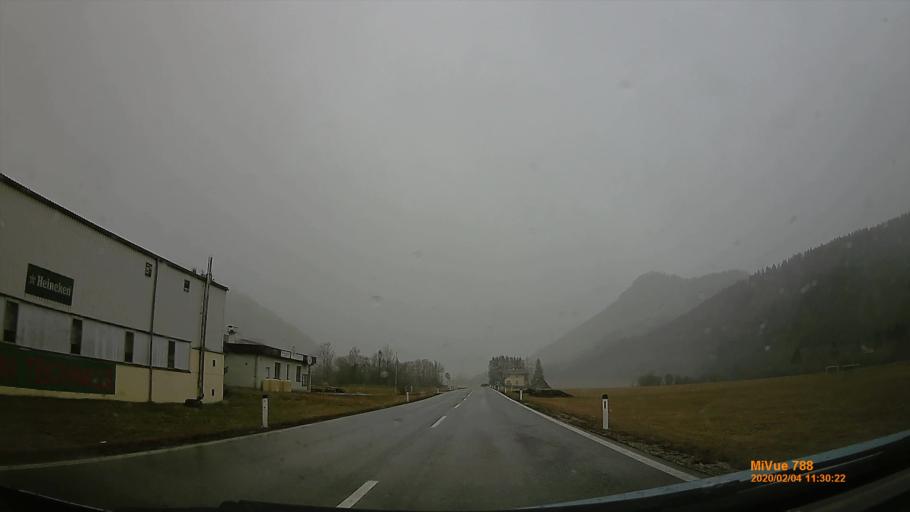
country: AT
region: Styria
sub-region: Politischer Bezirk Bruck-Muerzzuschlag
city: Kapellen
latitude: 47.6553
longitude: 15.6030
